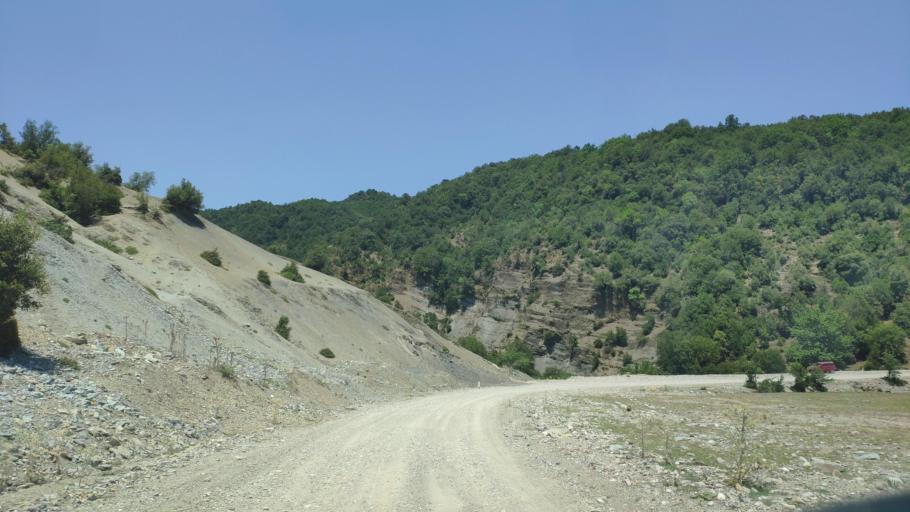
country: GR
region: Thessaly
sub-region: Nomos Kardhitsas
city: Anthiro
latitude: 39.1669
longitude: 21.3701
